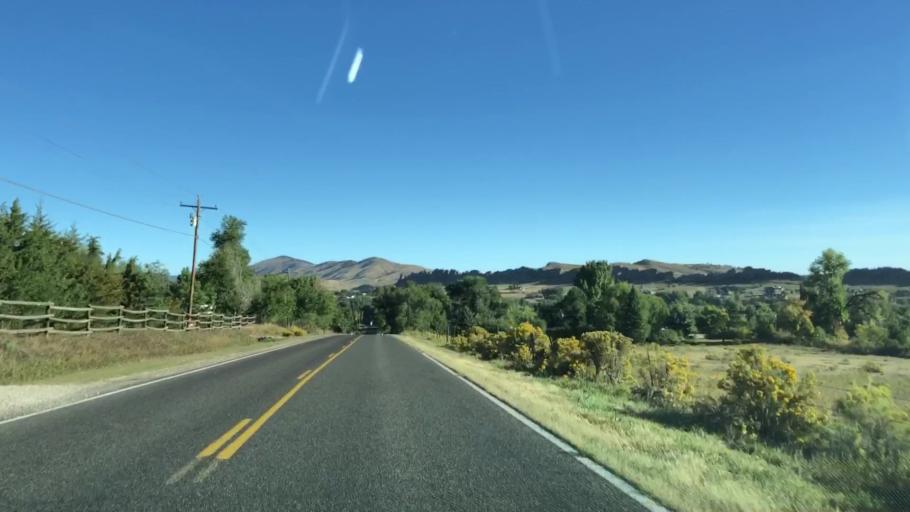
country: US
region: Colorado
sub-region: Larimer County
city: Loveland
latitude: 40.4061
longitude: -105.1688
